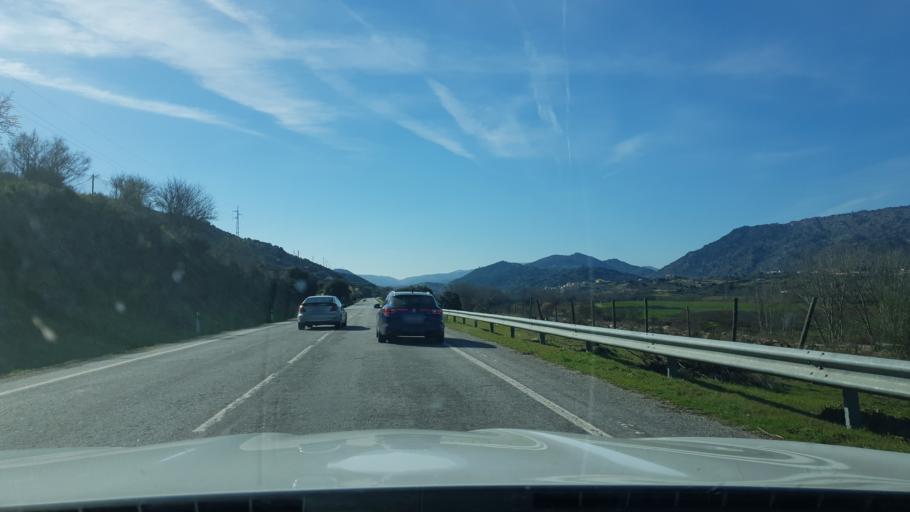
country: PT
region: Braganca
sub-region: Torre de Moncorvo
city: Torre de Moncorvo
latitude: 41.1978
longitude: -7.0958
